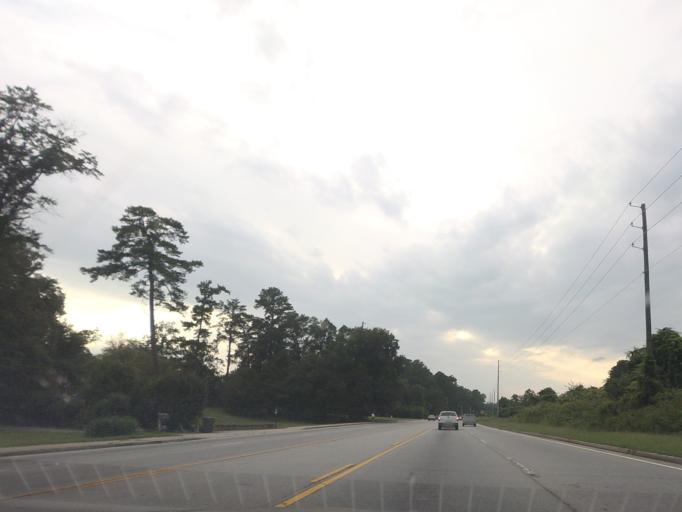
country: US
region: Georgia
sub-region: Bibb County
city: Macon
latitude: 32.8788
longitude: -83.7211
